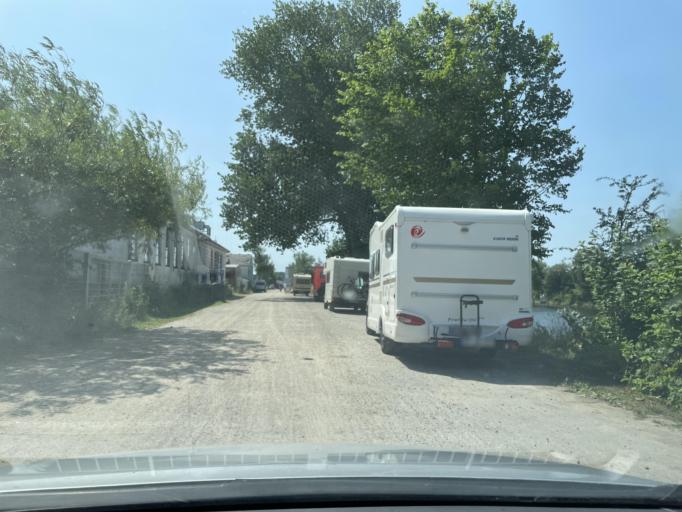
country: DE
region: Schleswig-Holstein
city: Flensburg
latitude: 54.8044
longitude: 9.4433
